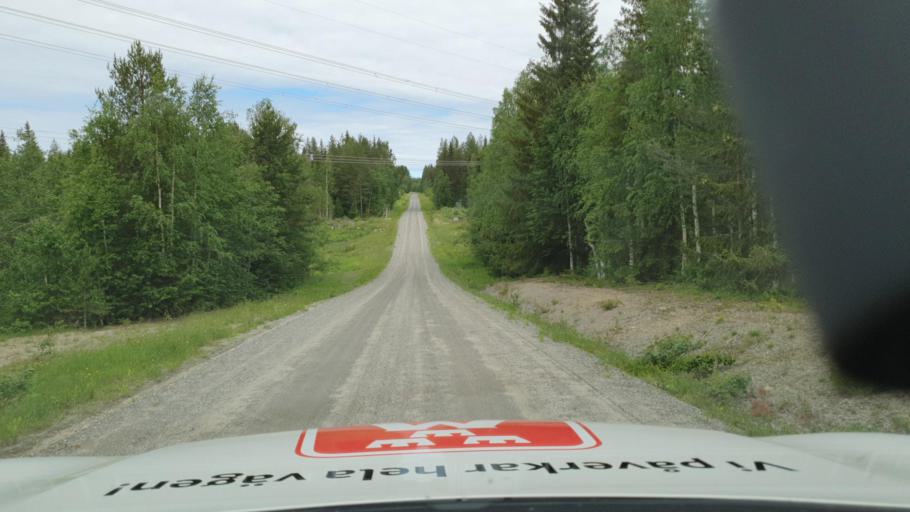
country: SE
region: Vaesterbotten
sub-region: Skelleftea Kommun
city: Langsele
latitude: 64.4699
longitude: 20.2675
